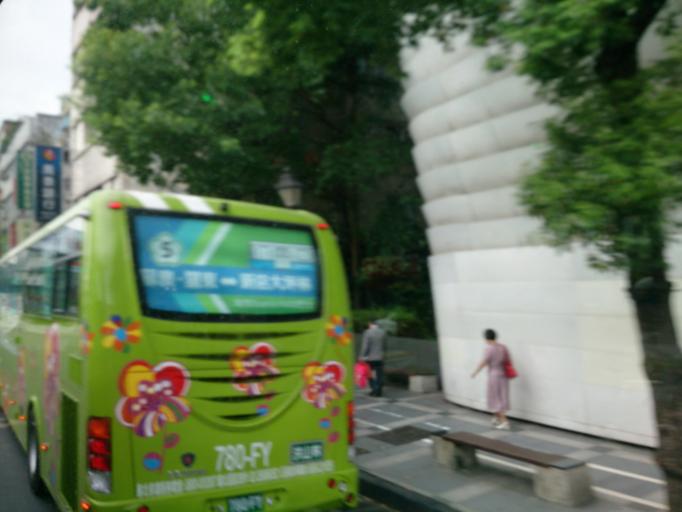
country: TW
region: Taipei
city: Taipei
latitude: 24.9838
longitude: 121.5413
